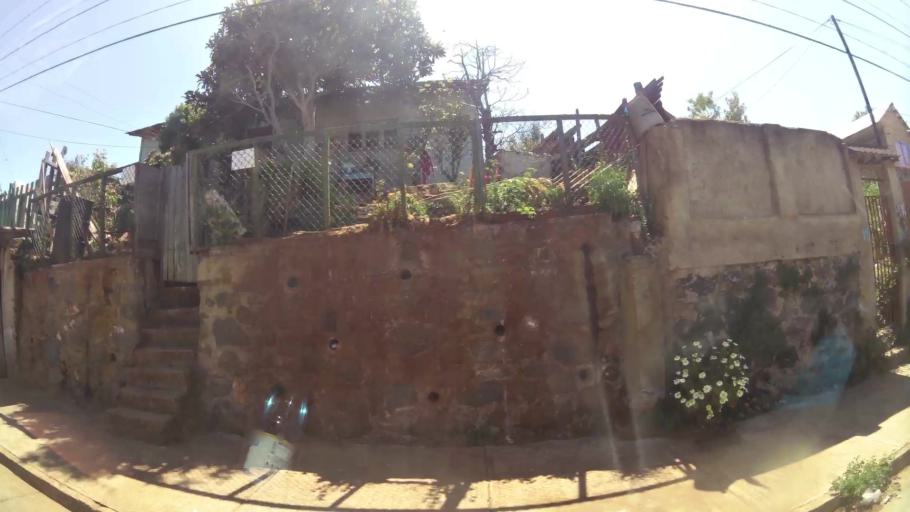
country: CL
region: Valparaiso
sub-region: Provincia de Valparaiso
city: Valparaiso
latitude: -33.0377
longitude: -71.6481
